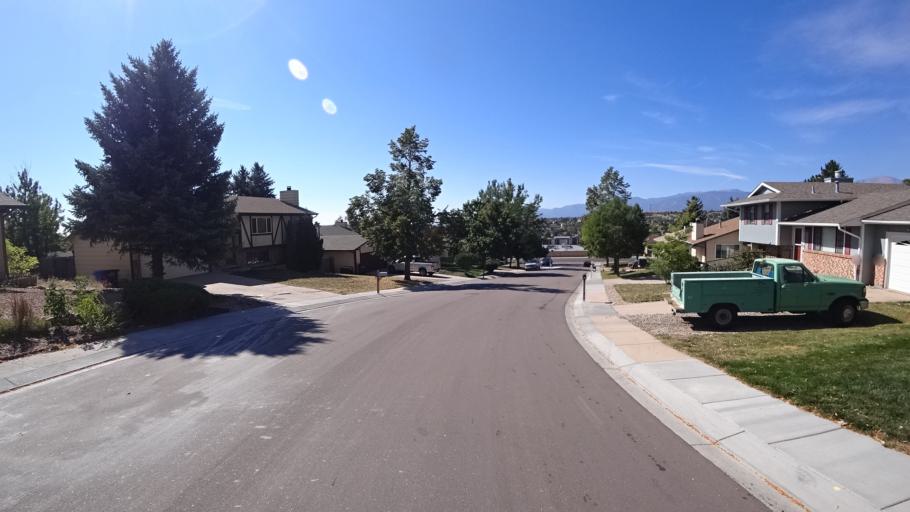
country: US
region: Colorado
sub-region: El Paso County
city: Colorado Springs
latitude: 38.9098
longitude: -104.7809
